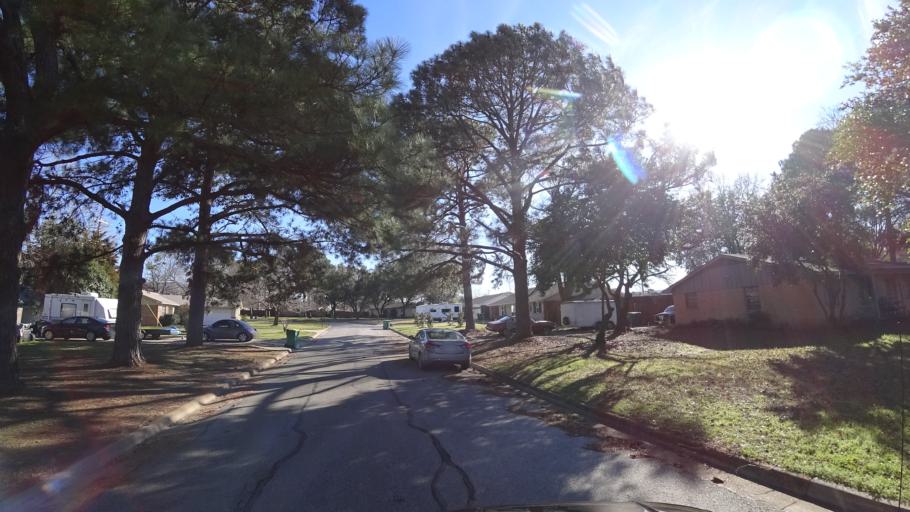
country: US
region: Texas
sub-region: Denton County
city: Lewisville
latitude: 33.0734
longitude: -97.0145
